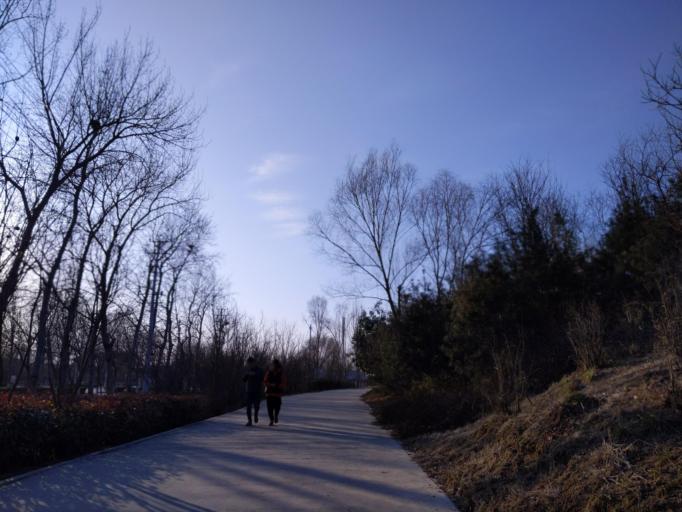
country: CN
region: Henan Sheng
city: Puyang
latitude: 35.7665
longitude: 114.9964
